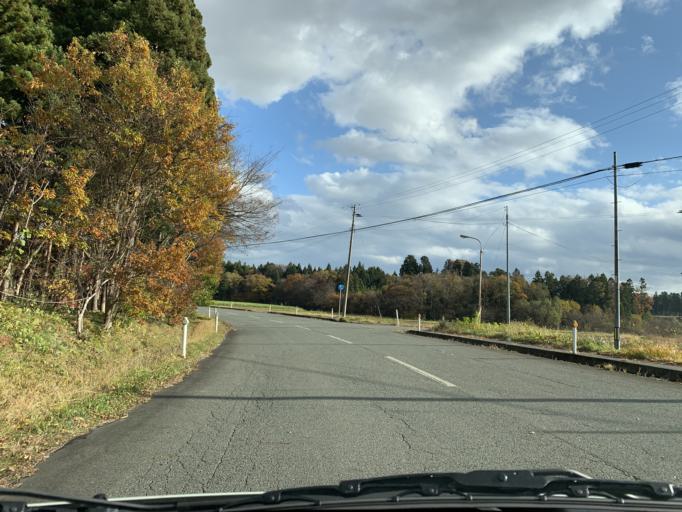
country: JP
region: Iwate
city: Mizusawa
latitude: 39.1121
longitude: 141.0193
